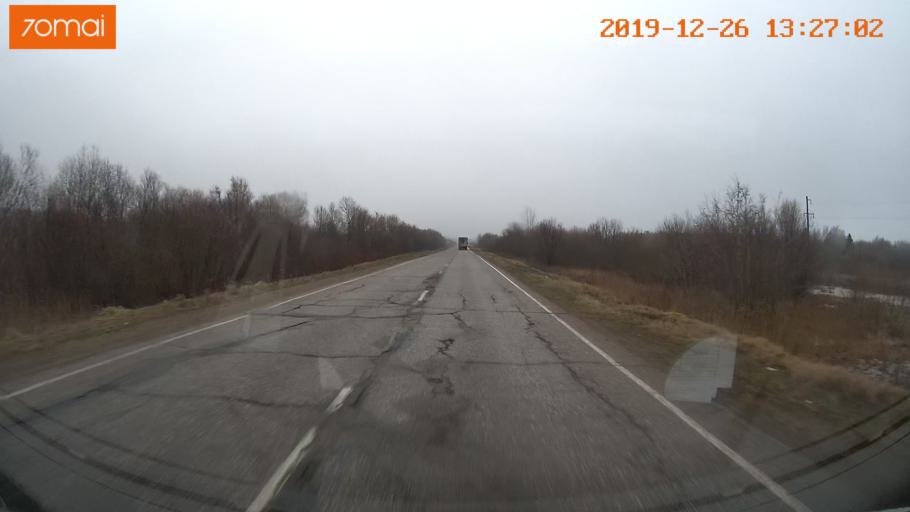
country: RU
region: Vologda
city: Cherepovets
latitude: 58.8569
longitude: 38.2355
